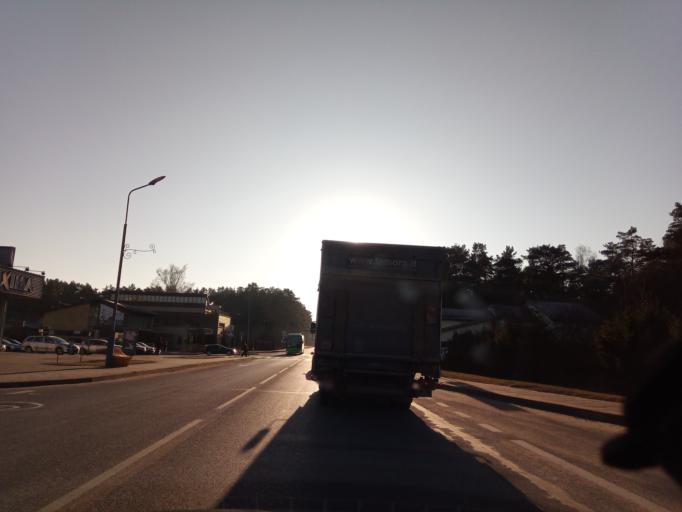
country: LT
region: Alytaus apskritis
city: Druskininkai
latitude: 54.0213
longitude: 24.0013
